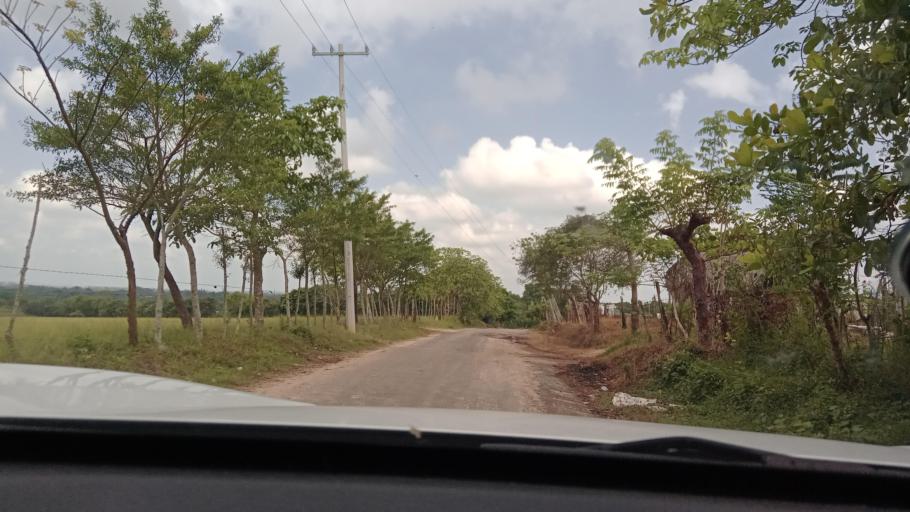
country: MX
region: Veracruz
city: Las Choapas
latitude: 17.8886
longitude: -94.1115
